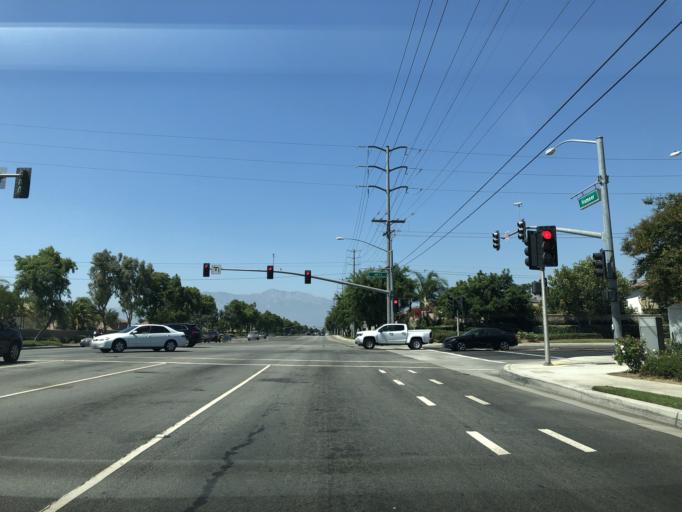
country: US
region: California
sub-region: Riverside County
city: Norco
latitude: 33.9641
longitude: -117.5582
